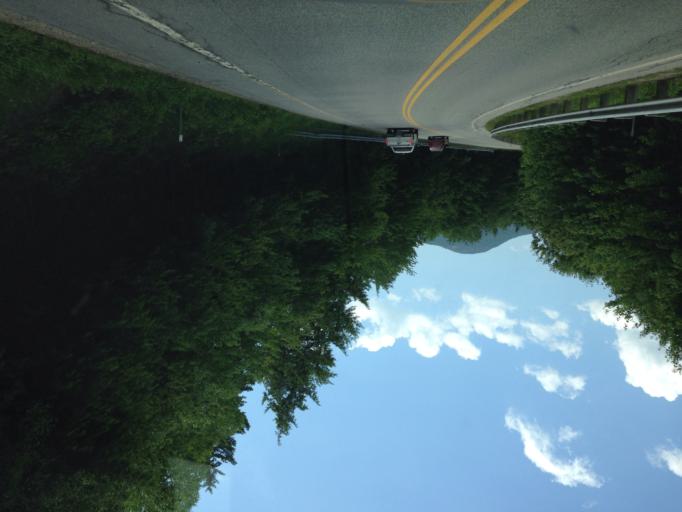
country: US
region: New Hampshire
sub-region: Carroll County
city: Sandwich
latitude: 44.0062
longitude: -71.4245
